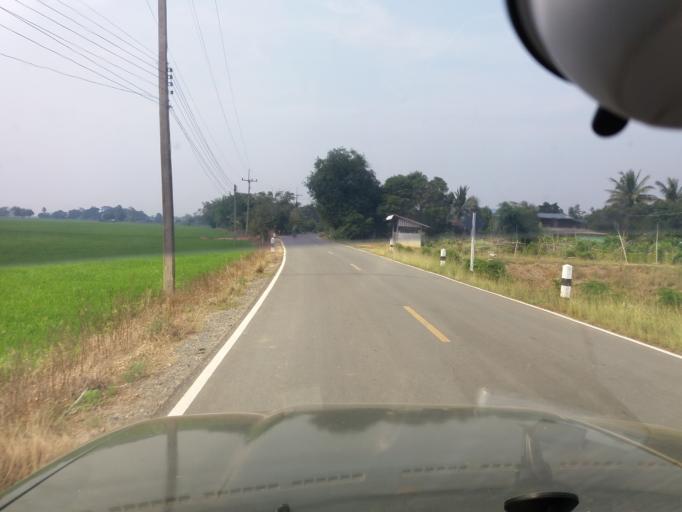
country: TH
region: Suphan Buri
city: Doem Bang Nang Buat
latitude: 14.8919
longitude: 100.1745
